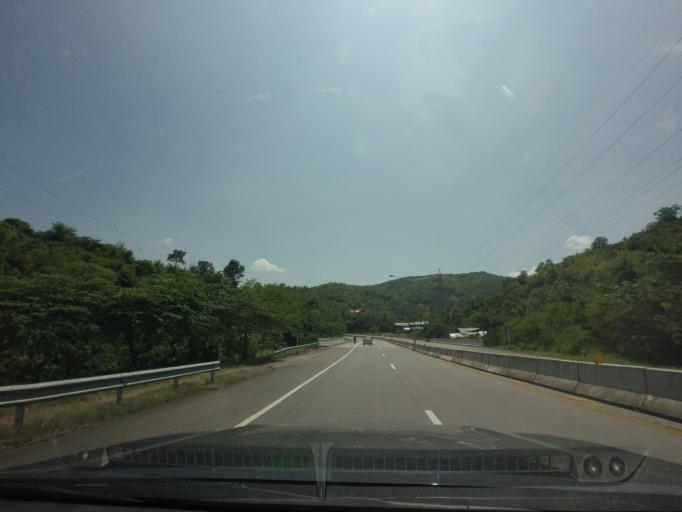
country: TH
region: Phetchabun
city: Lom Sak
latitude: 16.7651
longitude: 101.1406
